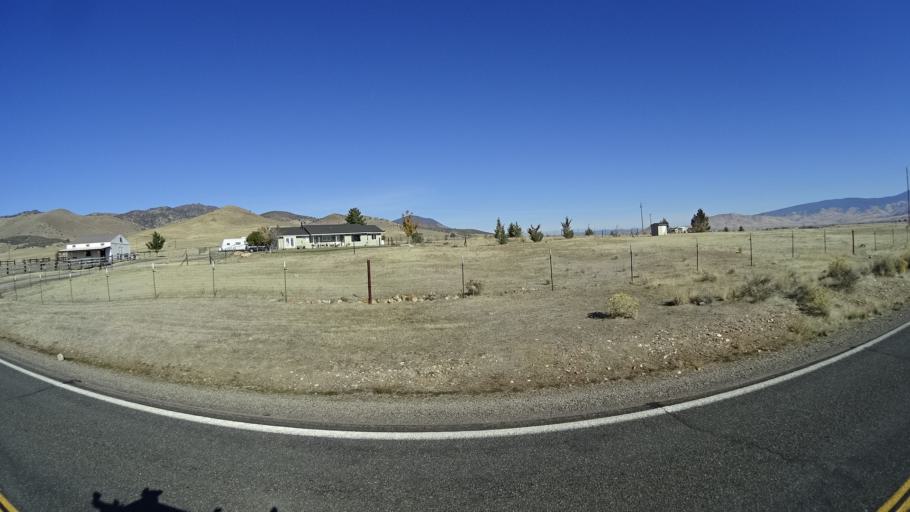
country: US
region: California
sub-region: Siskiyou County
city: Montague
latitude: 41.7712
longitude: -122.5227
